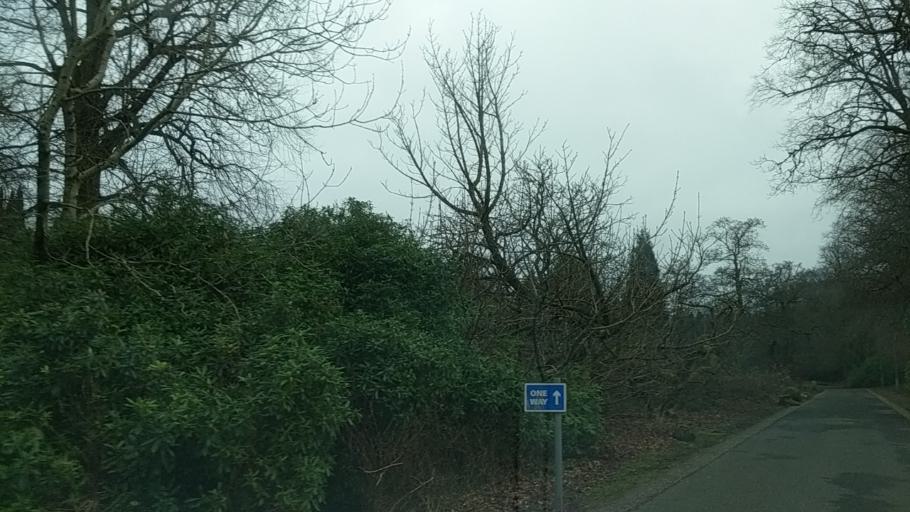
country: GB
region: Scotland
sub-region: South Lanarkshire
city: East Kilbride
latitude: 55.7497
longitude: -4.1478
